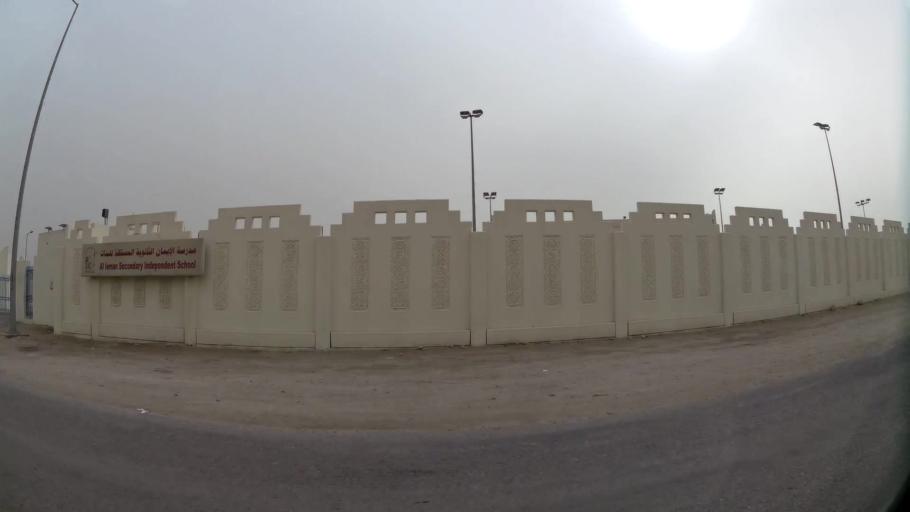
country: QA
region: Baladiyat ad Dawhah
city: Doha
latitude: 25.2435
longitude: 51.5097
